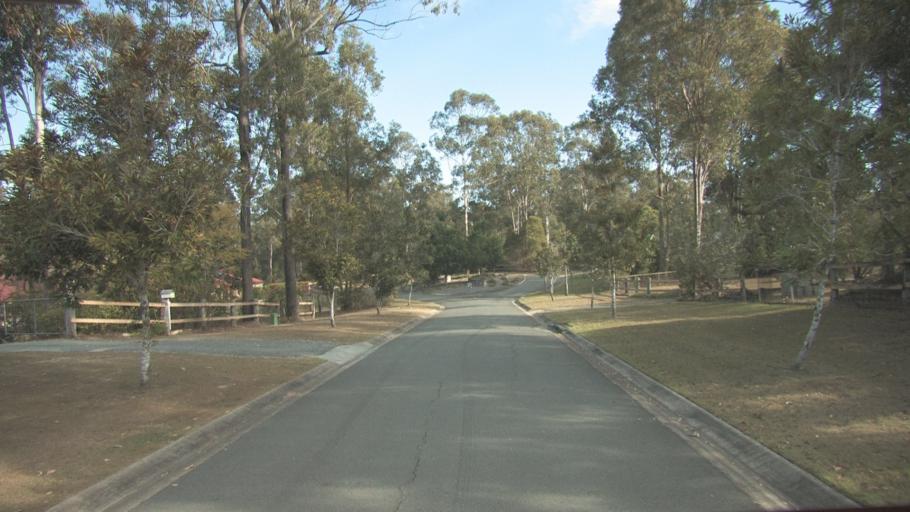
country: AU
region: Queensland
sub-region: Logan
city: North Maclean
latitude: -27.8038
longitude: 152.9682
